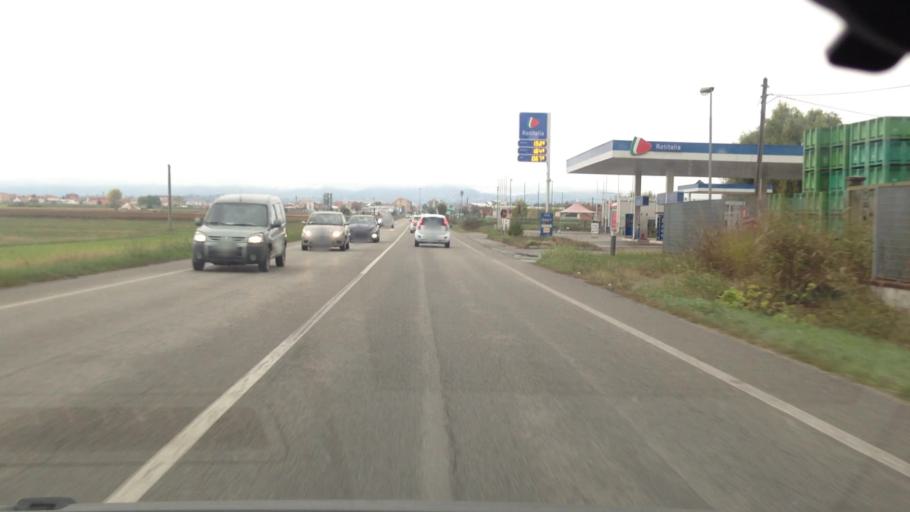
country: IT
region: Piedmont
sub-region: Provincia di Torino
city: Riva Presso Chieri
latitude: 44.9953
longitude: 7.8575
